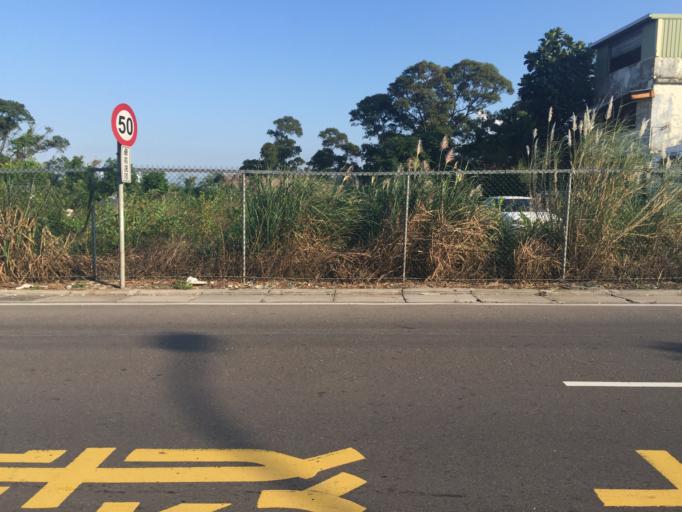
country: TW
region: Taiwan
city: Daxi
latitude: 24.9268
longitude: 121.2591
